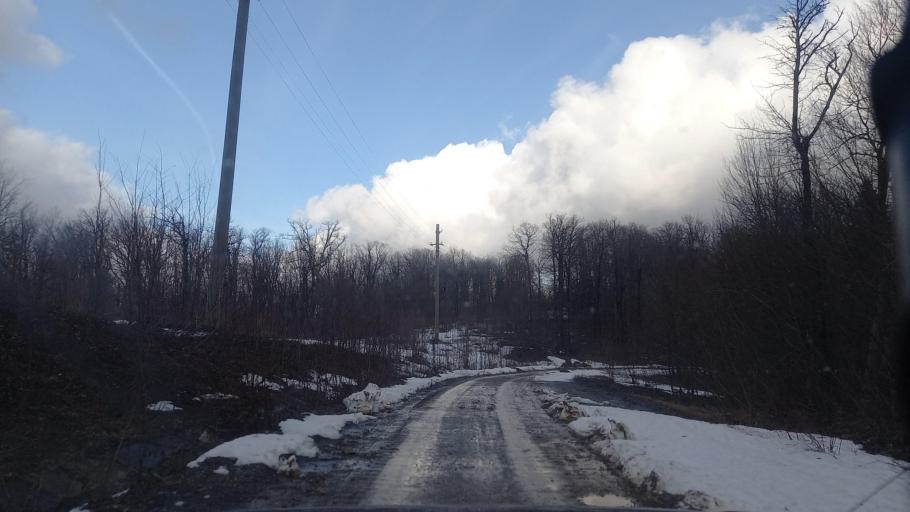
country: RU
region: Krasnodarskiy
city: Dzhubga
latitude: 44.5082
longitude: 38.7712
